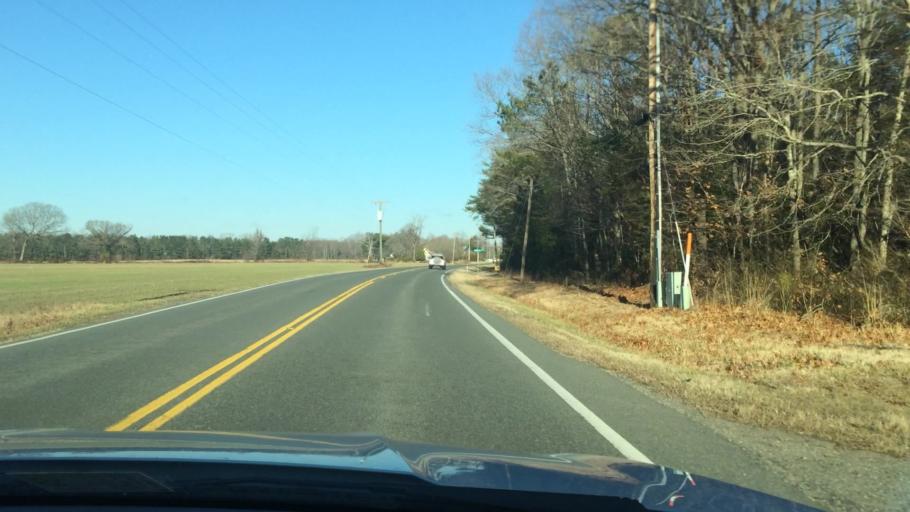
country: US
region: Virginia
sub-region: Lancaster County
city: Lancaster
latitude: 37.7551
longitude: -76.4155
